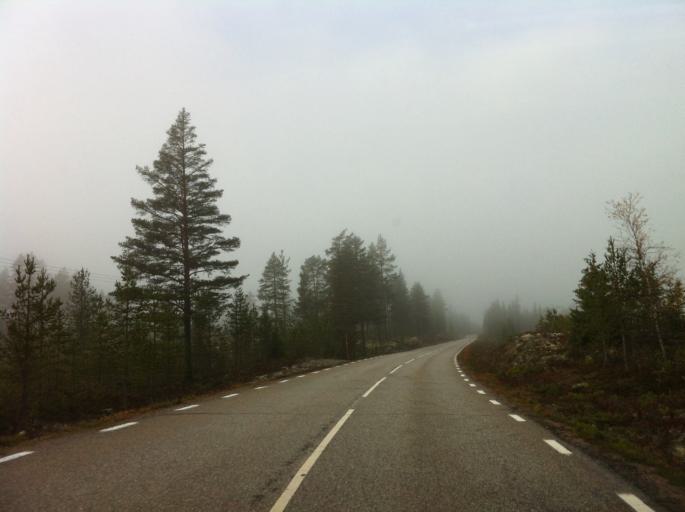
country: NO
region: Hedmark
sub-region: Engerdal
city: Engerdal
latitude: 61.9766
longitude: 12.4941
